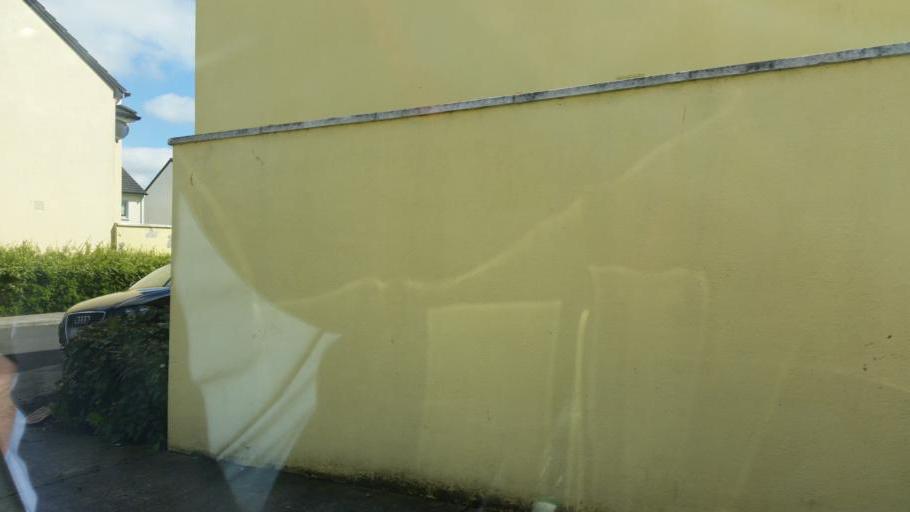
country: IE
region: Leinster
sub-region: Laois
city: Portlaoise
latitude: 53.0416
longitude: -7.2988
